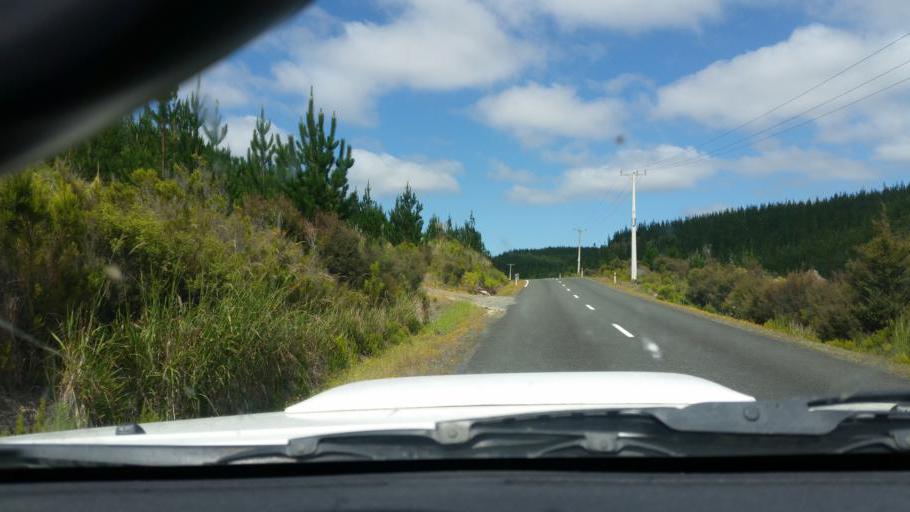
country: NZ
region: Northland
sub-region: Kaipara District
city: Dargaville
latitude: -35.8173
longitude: 173.7135
